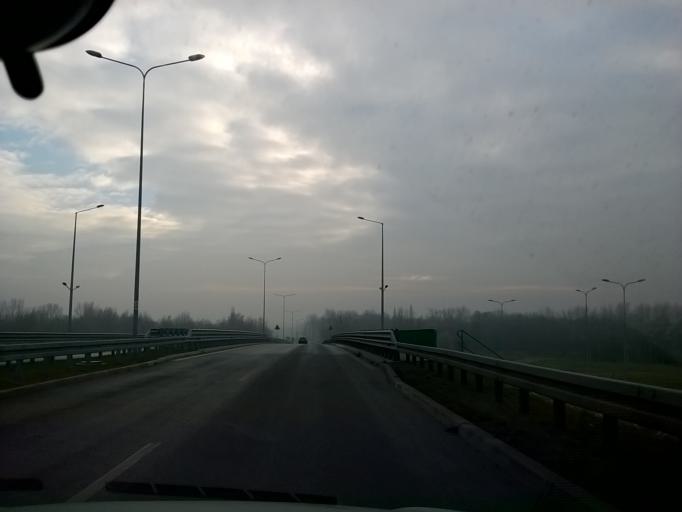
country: PL
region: Silesian Voivodeship
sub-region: Ruda Slaska
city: Ruda Slaska
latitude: 50.2836
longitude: 18.8481
